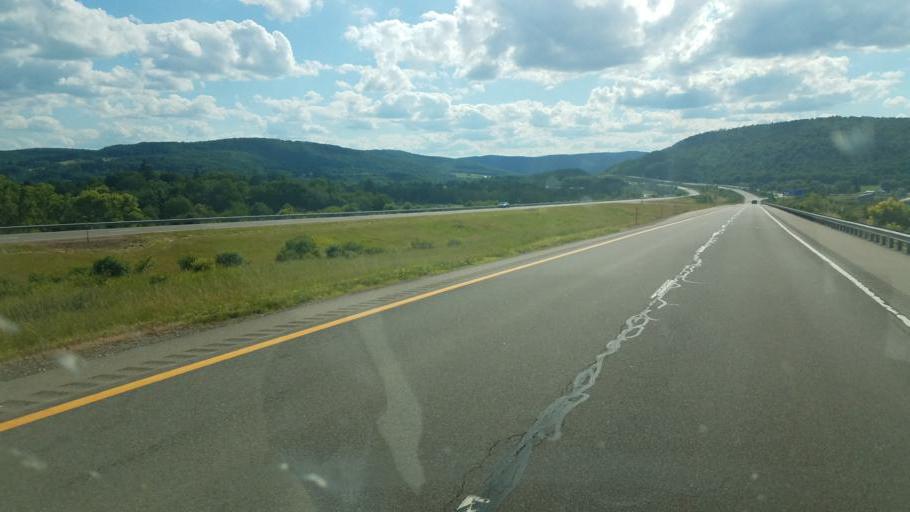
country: US
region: New York
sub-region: Allegany County
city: Cuba
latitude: 42.2254
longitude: -78.2645
